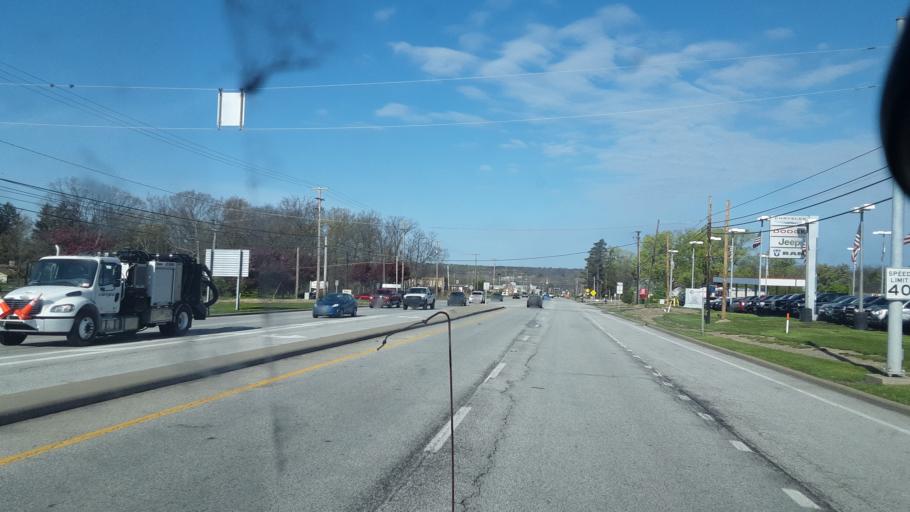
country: US
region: Ohio
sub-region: Medina County
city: Medina
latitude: 41.1363
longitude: -81.8022
